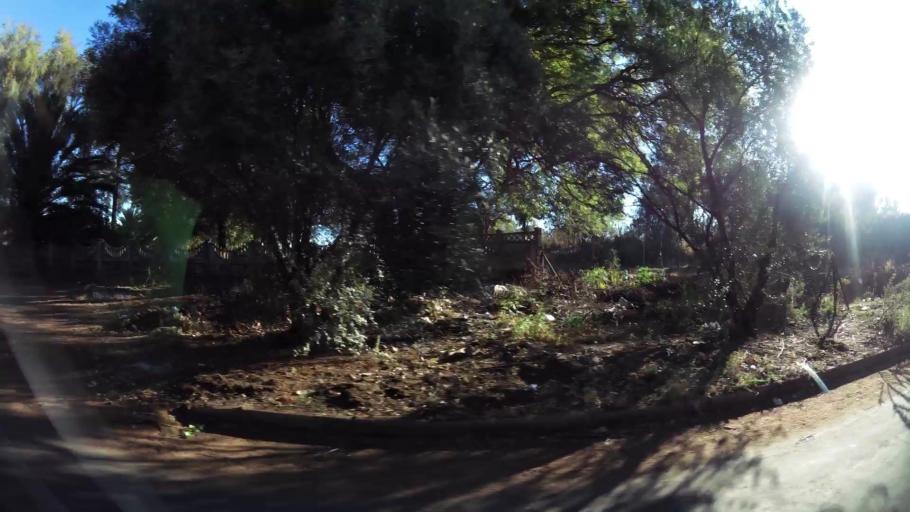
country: ZA
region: Northern Cape
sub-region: Frances Baard District Municipality
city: Kimberley
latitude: -28.7395
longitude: 24.7329
